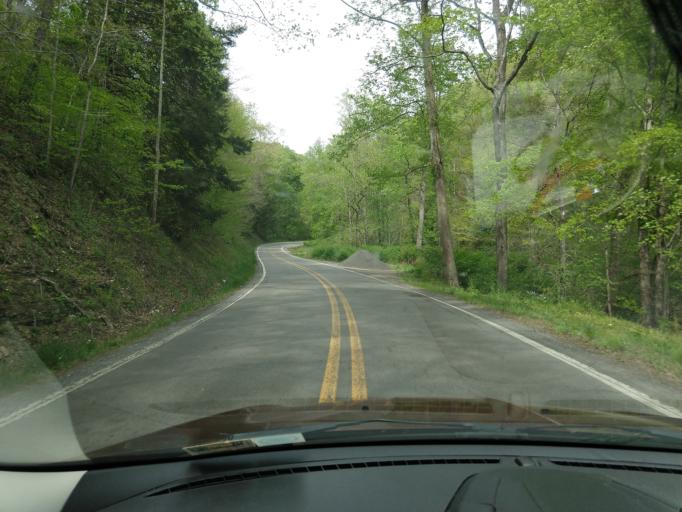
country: US
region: West Virginia
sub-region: McDowell County
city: Welch
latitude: 37.3568
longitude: -81.6603
